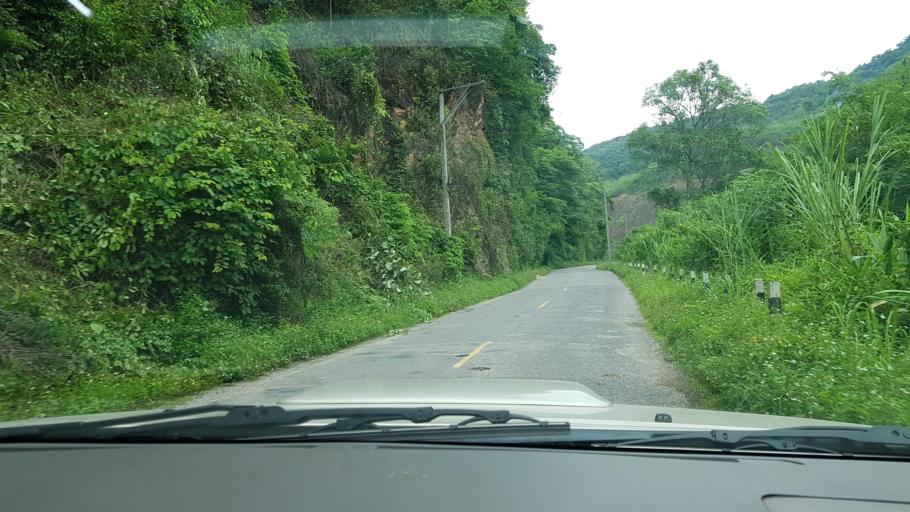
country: LA
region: Oudomxai
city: Muang La
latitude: 20.8765
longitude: 102.1459
